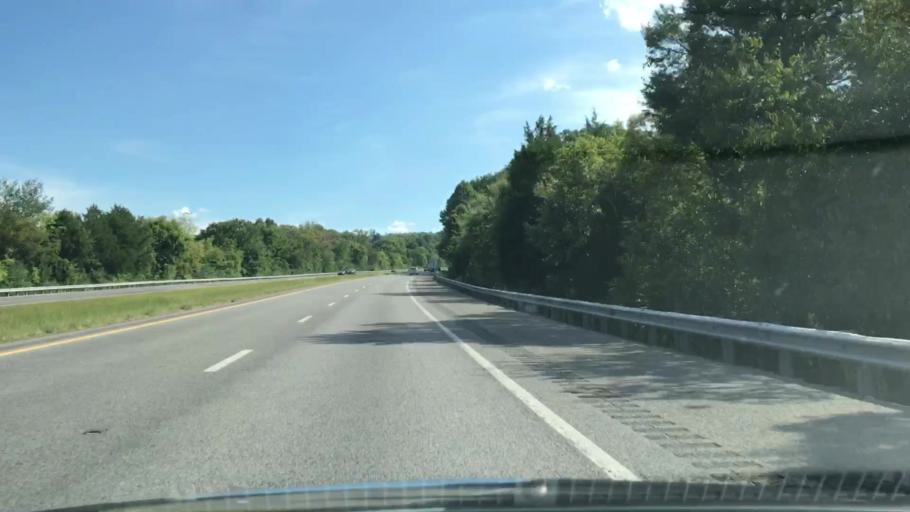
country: US
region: Alabama
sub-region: Limestone County
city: Ardmore
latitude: 35.1272
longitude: -86.8774
